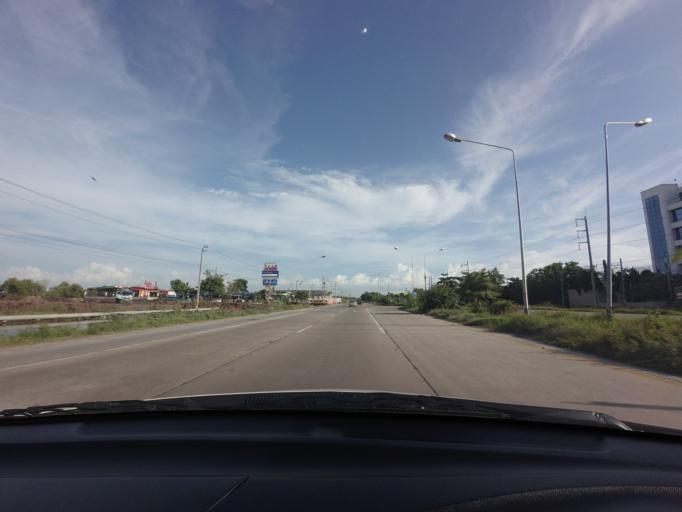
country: TH
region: Phra Nakhon Si Ayutthaya
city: Lat Bua Luang
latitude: 14.1256
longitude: 100.2895
